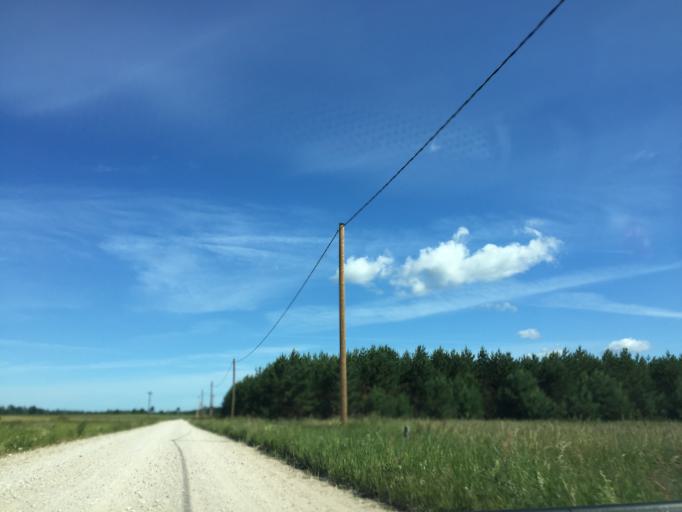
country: LV
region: Dundaga
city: Dundaga
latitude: 57.3445
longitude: 22.0278
